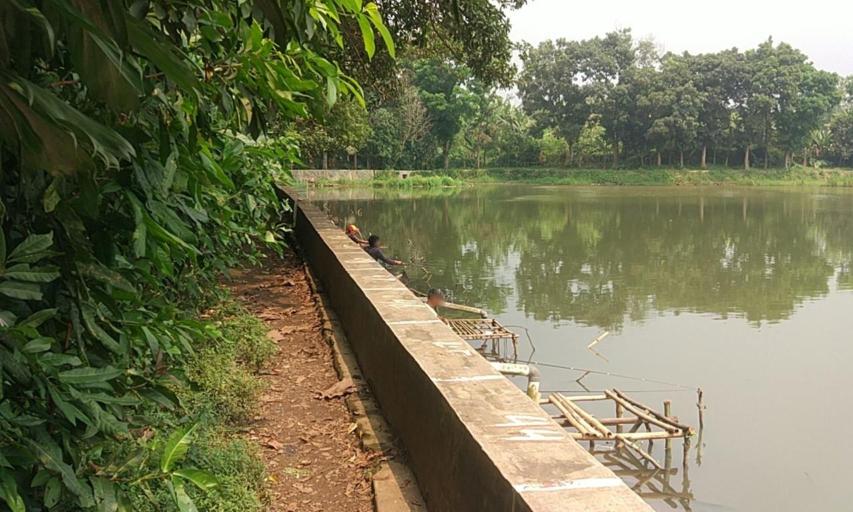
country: ID
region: West Java
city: Ciampea
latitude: -6.5331
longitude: 106.7291
